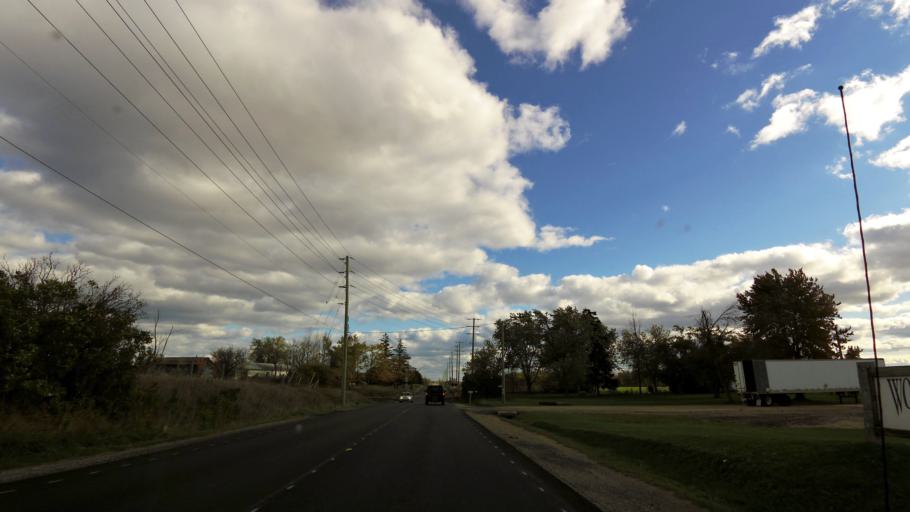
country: CA
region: Ontario
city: Burlington
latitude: 43.4395
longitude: -79.8175
